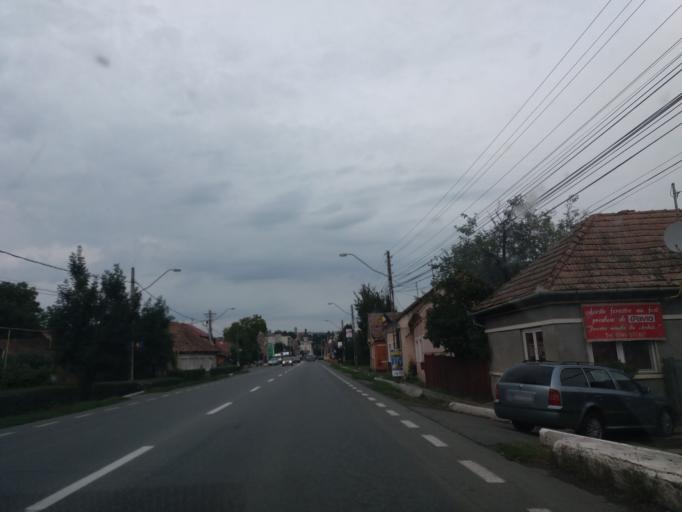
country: RO
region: Mures
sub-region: Municipiul Reghin
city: Reghin
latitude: 46.7691
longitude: 24.7039
